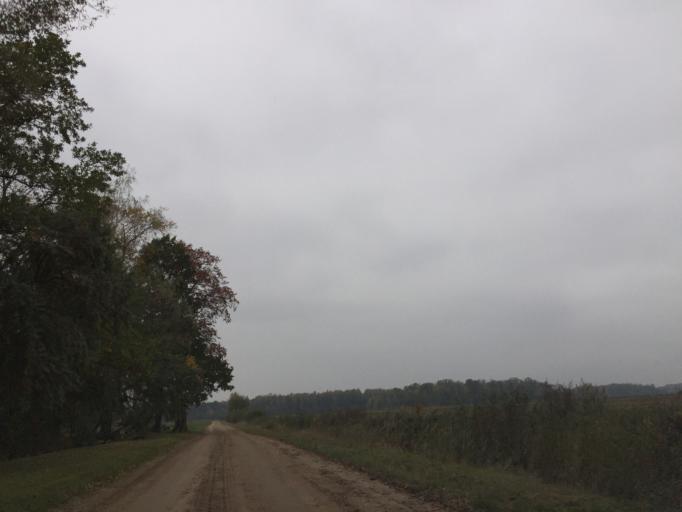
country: LV
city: Tireli
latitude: 56.6754
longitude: 23.4885
